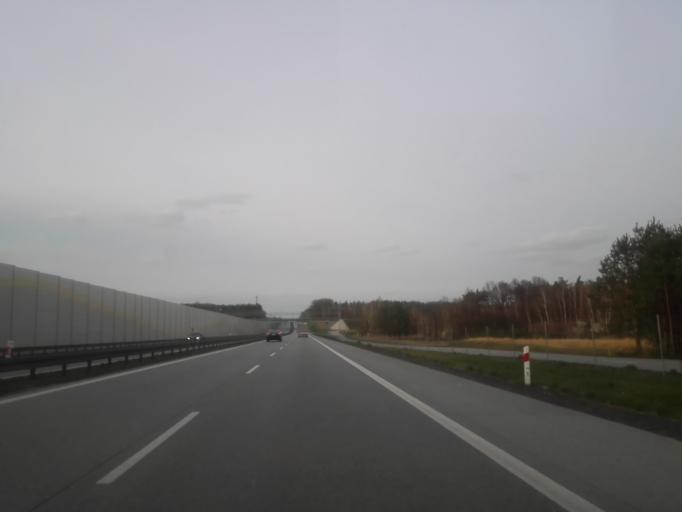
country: PL
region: Lodz Voivodeship
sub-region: Powiat rawski
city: Rawa Mazowiecka
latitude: 51.8121
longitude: 20.3099
